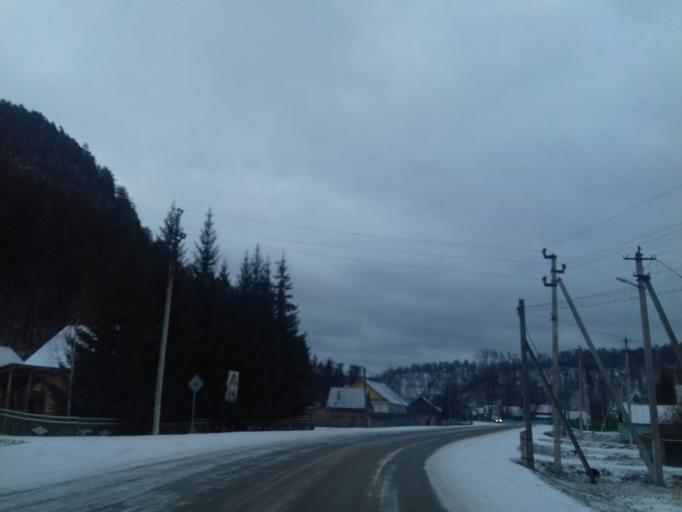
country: RU
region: Bashkortostan
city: Starosubkhangulovo
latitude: 53.1211
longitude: 57.4223
